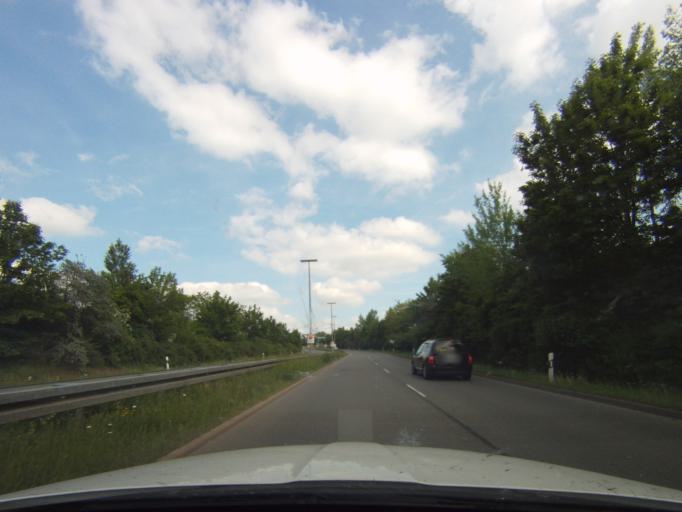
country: DE
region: Thuringia
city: Gera
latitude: 50.8617
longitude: 12.0886
